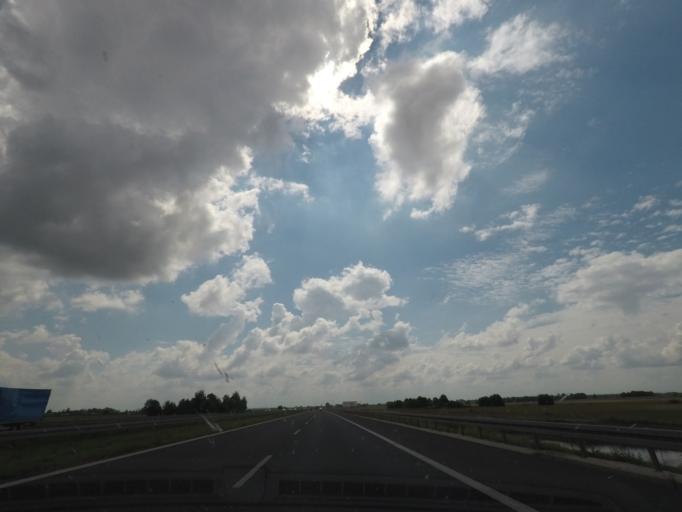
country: PL
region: Lodz Voivodeship
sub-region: Powiat zgierski
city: Strykow
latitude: 51.9899
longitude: 19.5526
